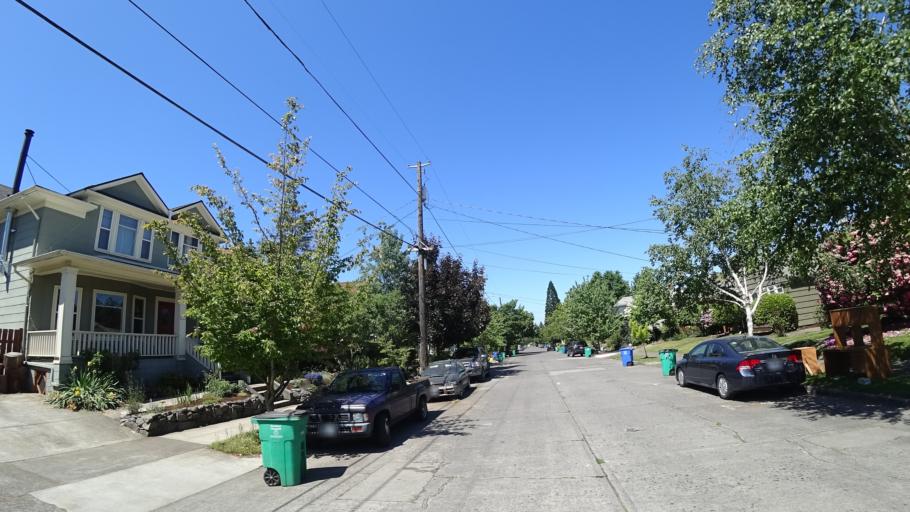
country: US
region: Oregon
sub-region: Multnomah County
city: Portland
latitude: 45.5635
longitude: -122.6481
